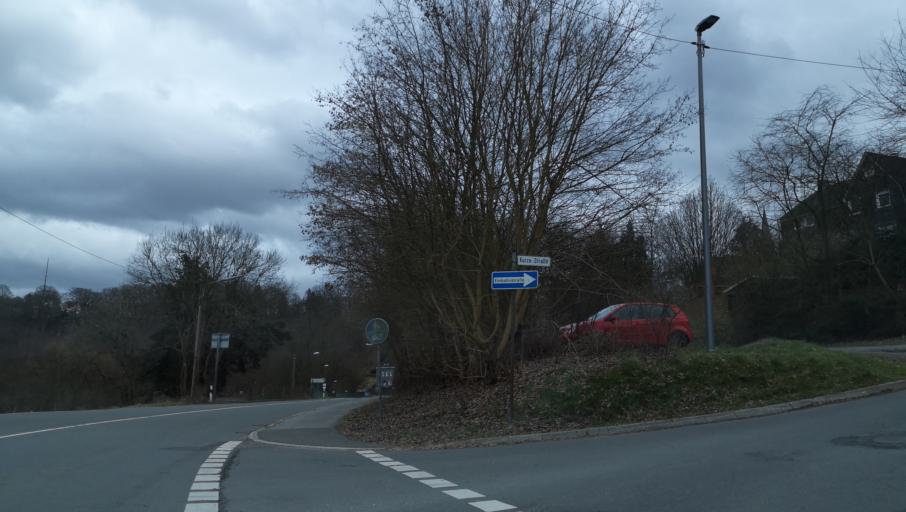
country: DE
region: North Rhine-Westphalia
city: Radevormwald
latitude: 51.2227
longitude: 7.3101
